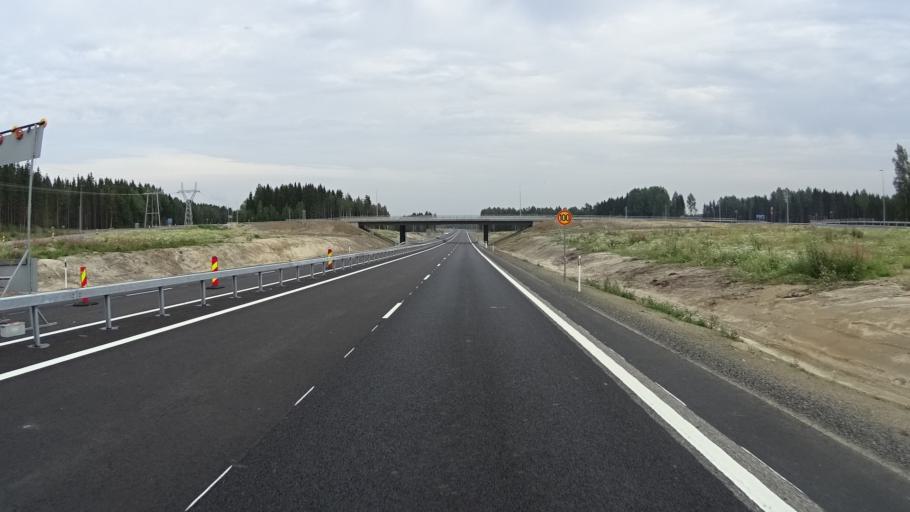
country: FI
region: South Karelia
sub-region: Lappeenranta
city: Luumaeki
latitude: 60.9383
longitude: 27.7035
